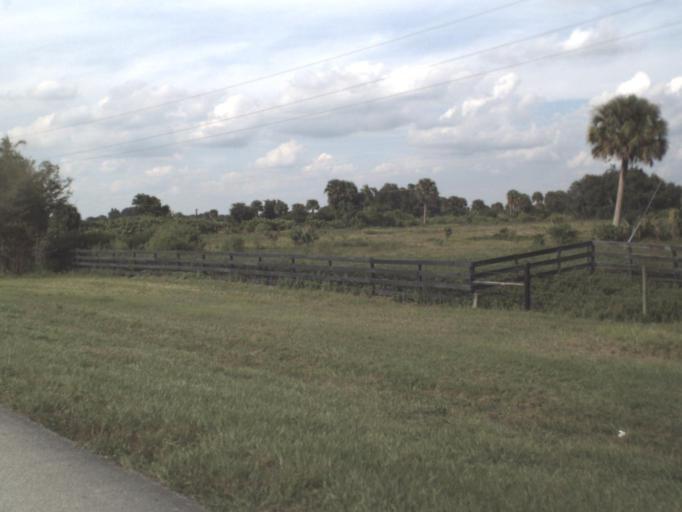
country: US
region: Florida
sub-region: Okeechobee County
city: Taylor Creek
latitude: 27.2106
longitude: -80.7552
